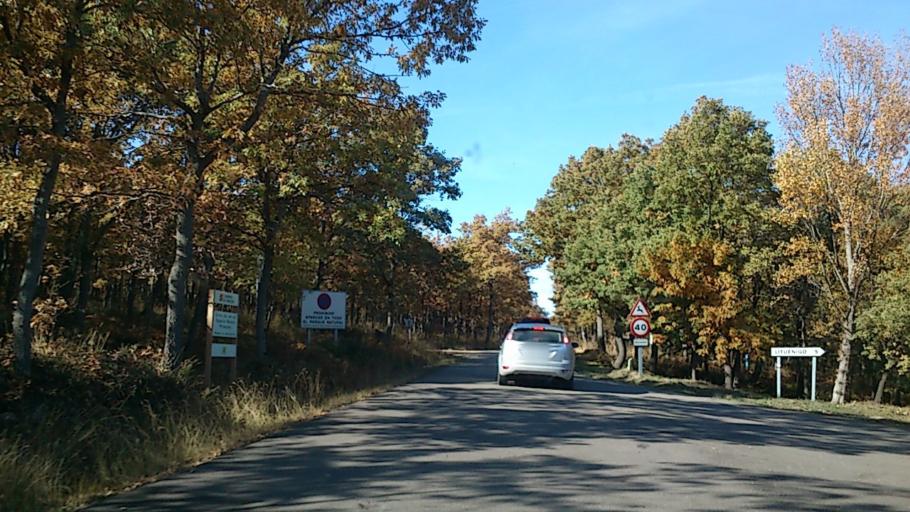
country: ES
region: Aragon
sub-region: Provincia de Zaragoza
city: Lituenigo
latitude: 41.8094
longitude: -1.8029
